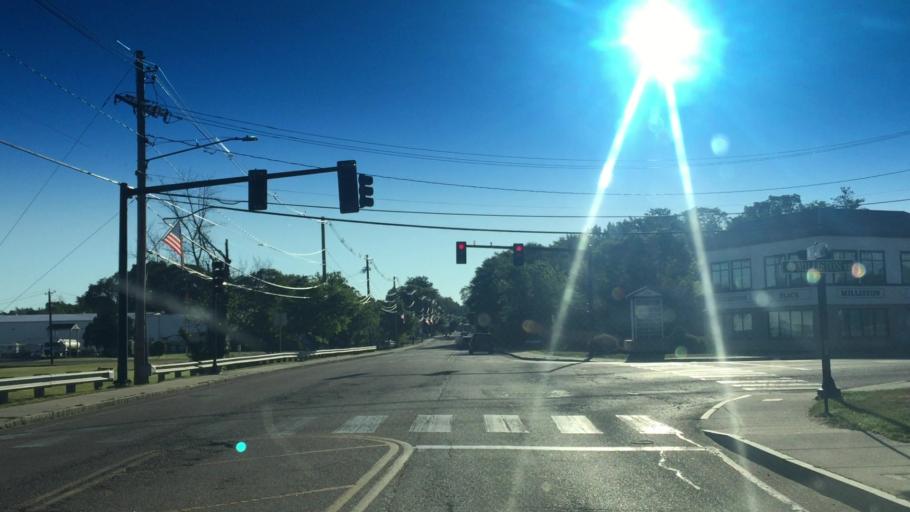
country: US
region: Massachusetts
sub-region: Norfolk County
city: Millis
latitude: 42.1685
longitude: -71.3545
